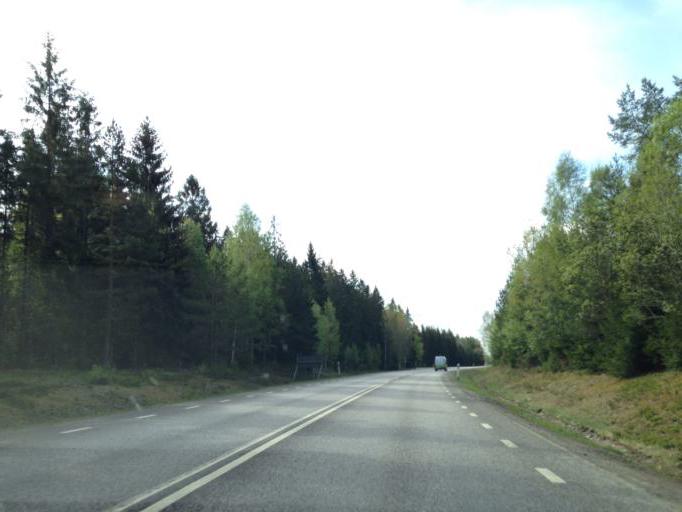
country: SE
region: Soedermanland
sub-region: Nykopings Kommun
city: Svalsta
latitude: 58.8489
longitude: 16.9217
